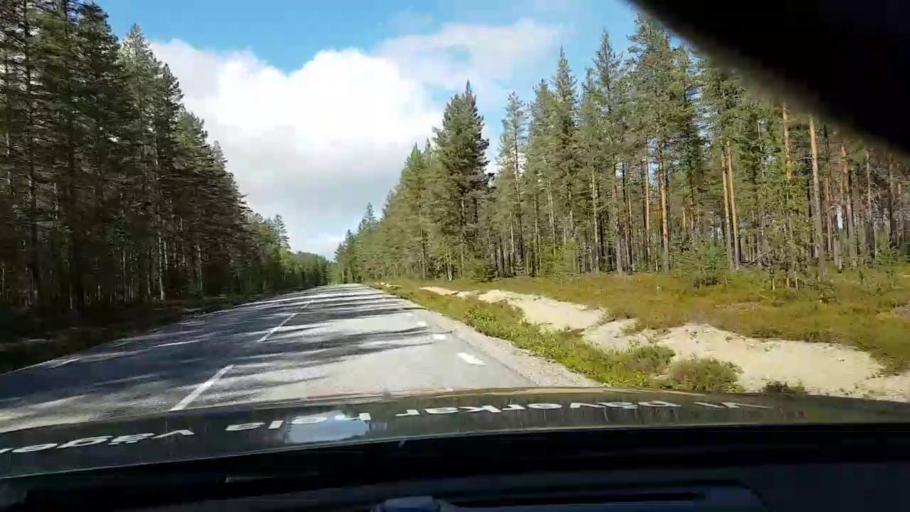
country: SE
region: Vaesternorrland
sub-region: OErnskoeldsviks Kommun
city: Bredbyn
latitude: 63.6653
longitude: 17.8346
